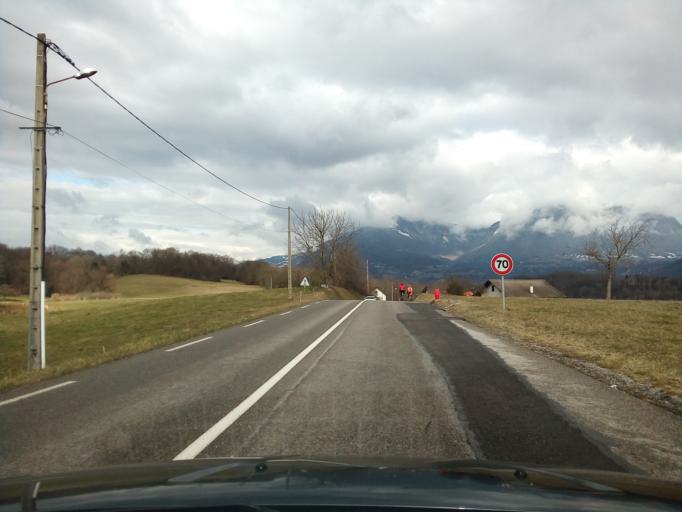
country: FR
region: Rhone-Alpes
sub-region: Departement de la Savoie
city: Saint-Baldoph
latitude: 45.5372
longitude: 5.9572
